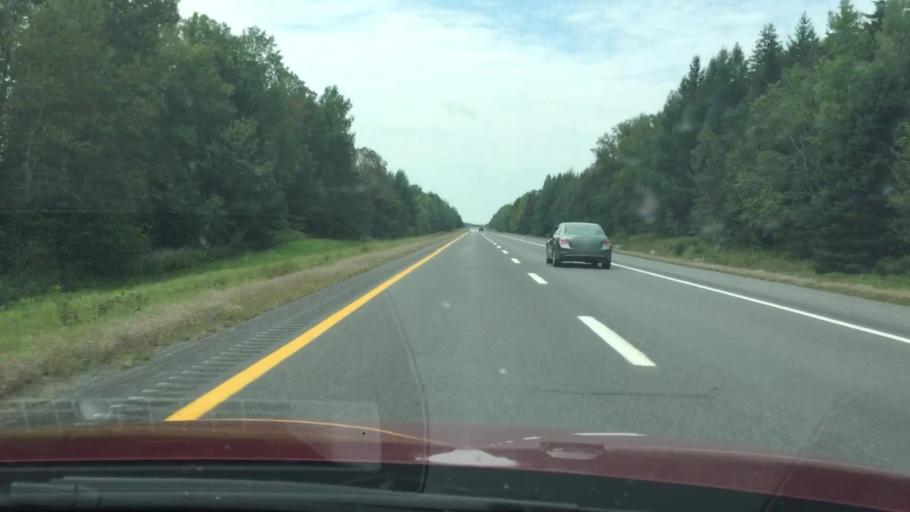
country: US
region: Maine
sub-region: Aroostook County
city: Houlton
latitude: 46.1371
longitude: -67.8783
